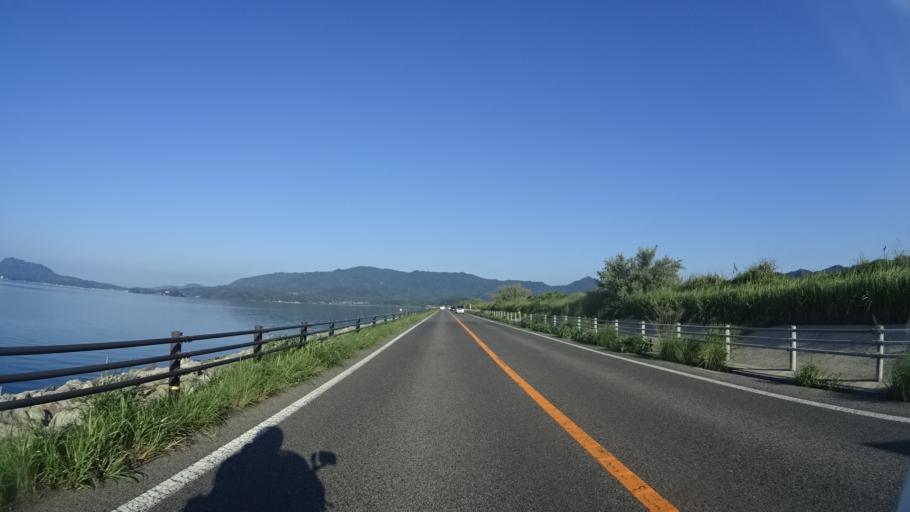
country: JP
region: Shimane
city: Sakaiminato
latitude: 35.5245
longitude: 133.1793
